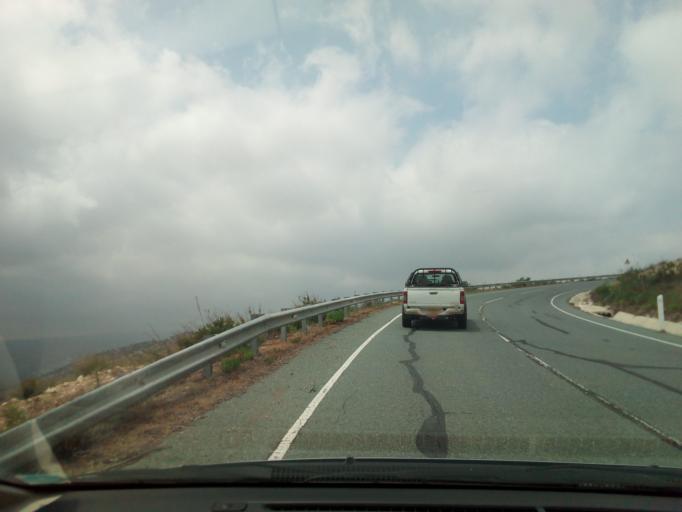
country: CY
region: Limassol
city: Pissouri
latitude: 34.7967
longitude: 32.6467
